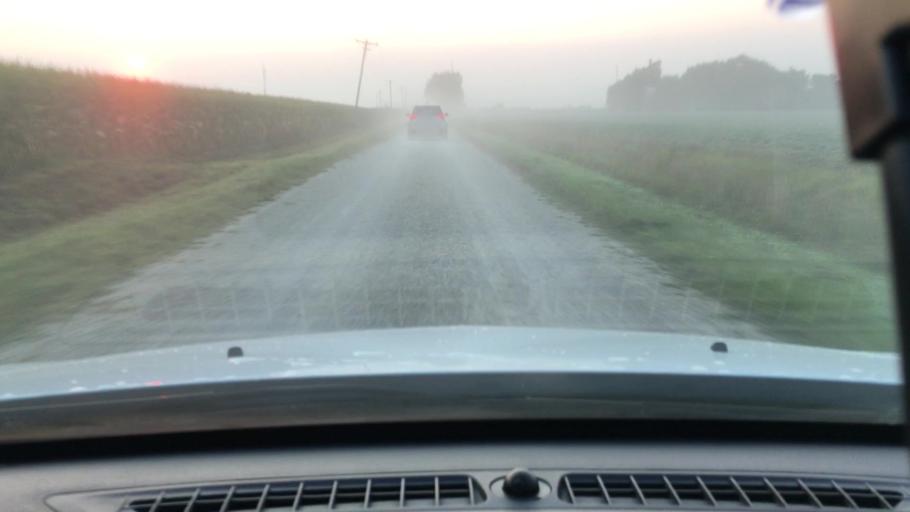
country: US
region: Illinois
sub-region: DeKalb County
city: Malta
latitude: 41.8632
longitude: -88.8338
